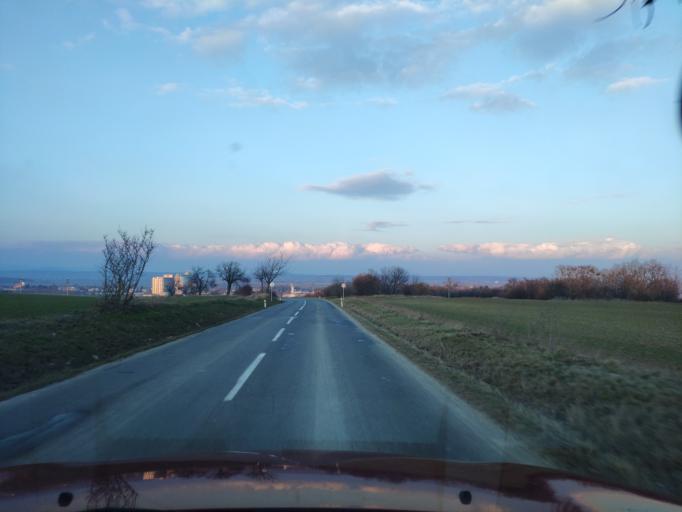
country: SK
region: Nitriansky
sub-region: Okres Nitra
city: Nitra
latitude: 48.2287
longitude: 18.1033
